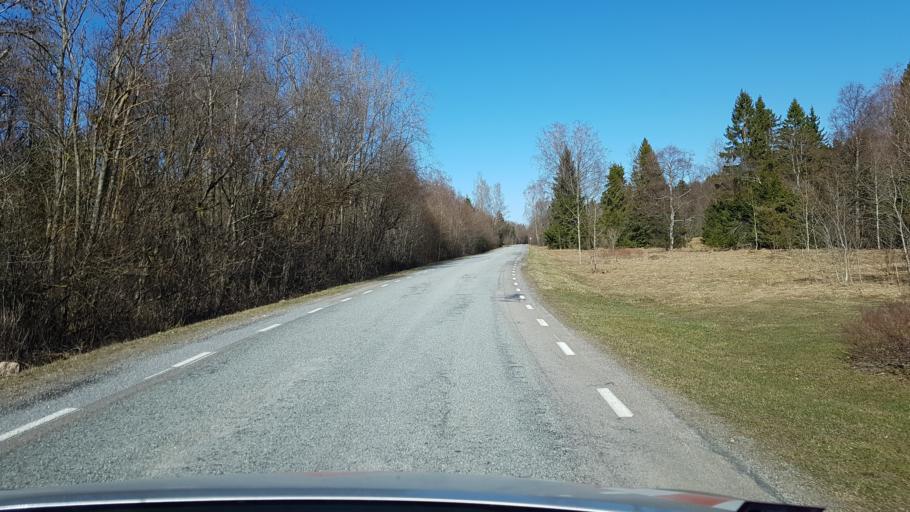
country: EE
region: Laeaene-Virumaa
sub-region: Someru vald
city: Someru
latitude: 59.3857
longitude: 26.4695
